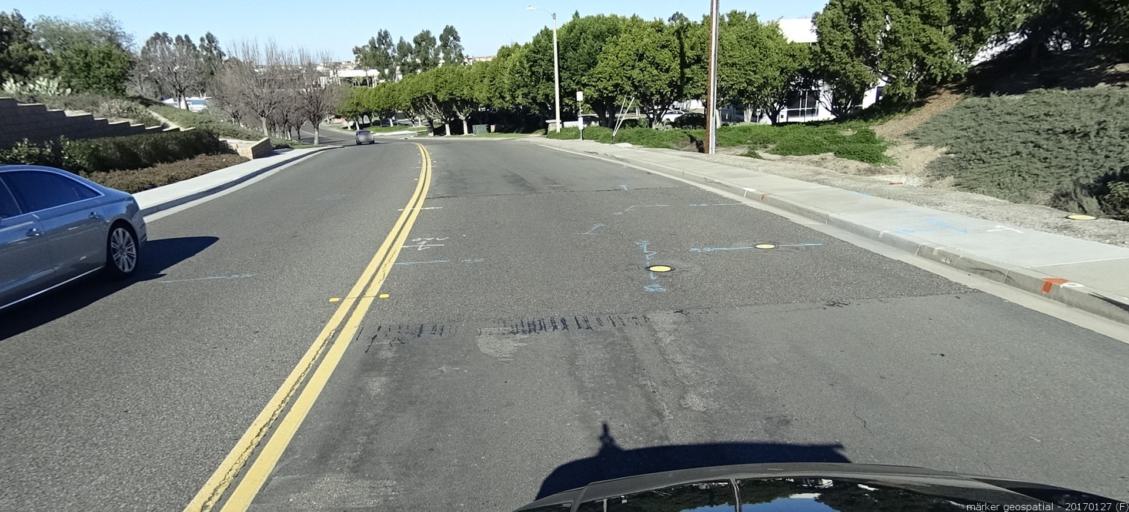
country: US
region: California
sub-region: Orange County
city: Foothill Ranch
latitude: 33.6627
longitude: -117.6637
